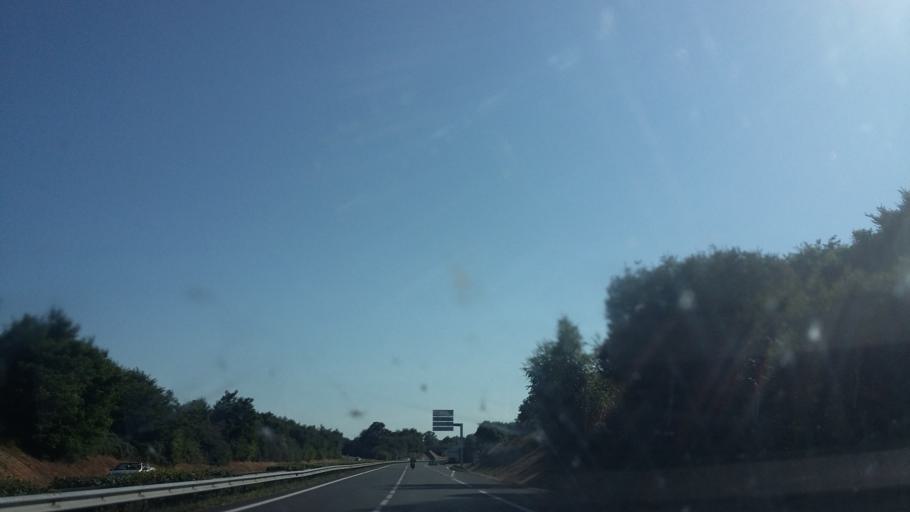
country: FR
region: Pays de la Loire
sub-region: Departement de la Vendee
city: Challans
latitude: 46.8610
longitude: -1.8773
